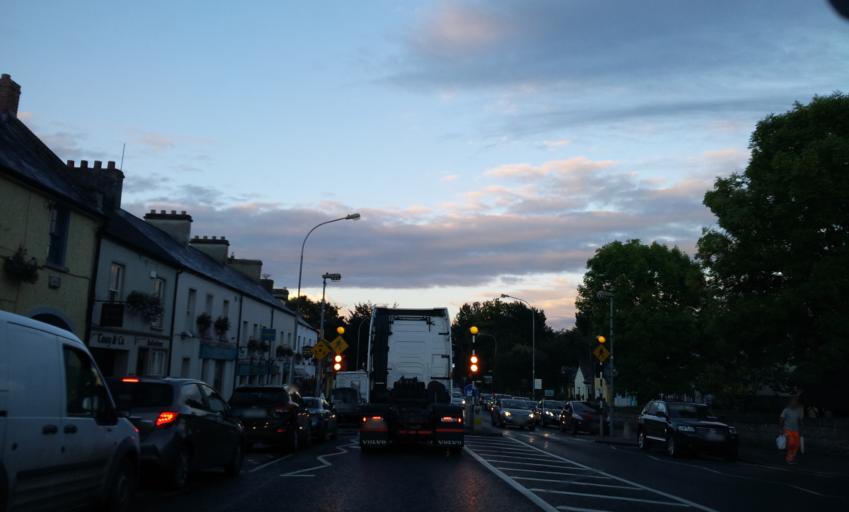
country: IE
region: Munster
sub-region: County Limerick
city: Adare
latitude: 52.5638
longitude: -8.7922
